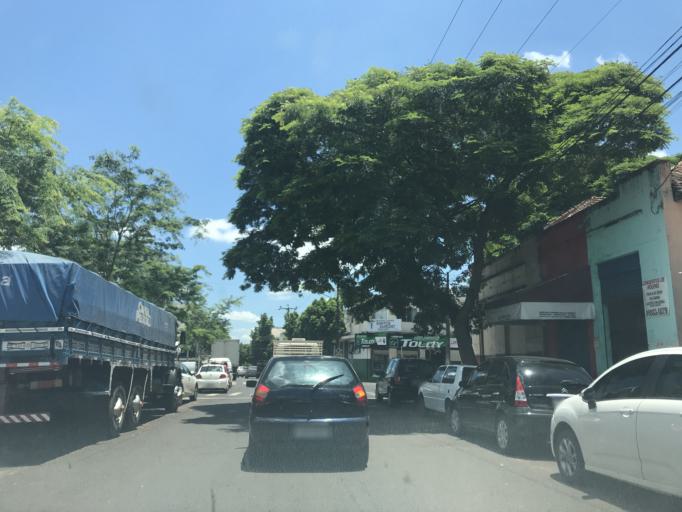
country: BR
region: Parana
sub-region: Marialva
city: Marialva
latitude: -23.4864
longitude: -51.7978
